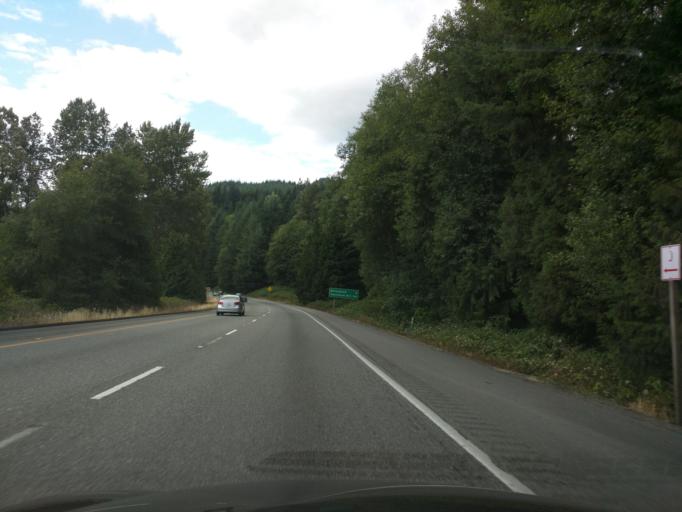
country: US
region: Washington
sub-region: Whatcom County
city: Sudden Valley
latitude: 48.6648
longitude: -122.3720
